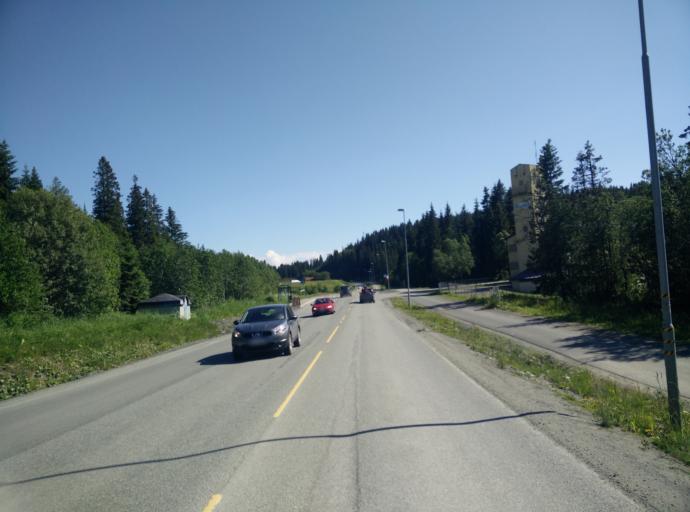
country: NO
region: Sor-Trondelag
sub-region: Trondheim
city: Trondheim
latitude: 63.3800
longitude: 10.3157
